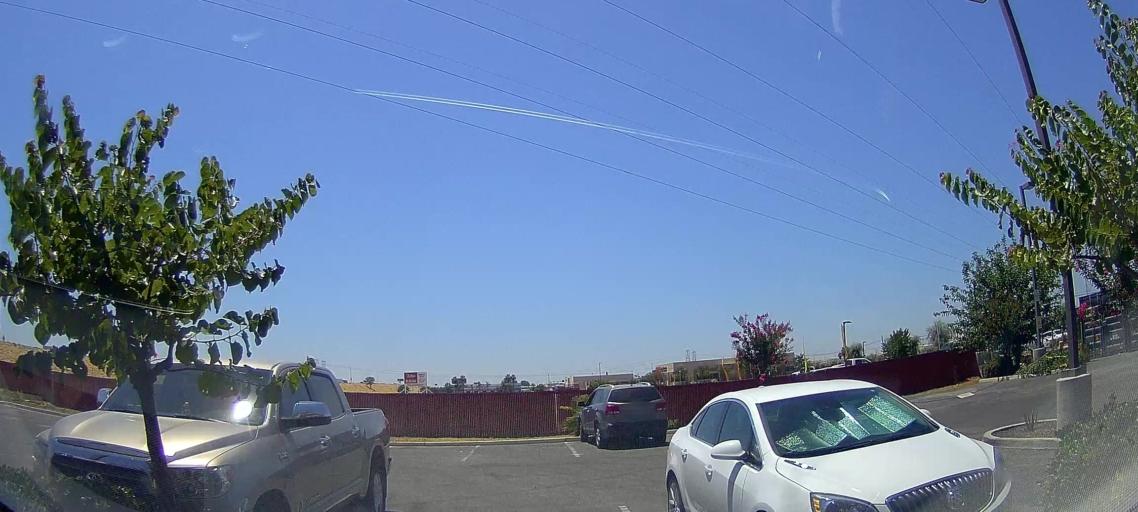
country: US
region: California
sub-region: Kern County
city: Lamont
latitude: 35.3535
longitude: -118.9159
